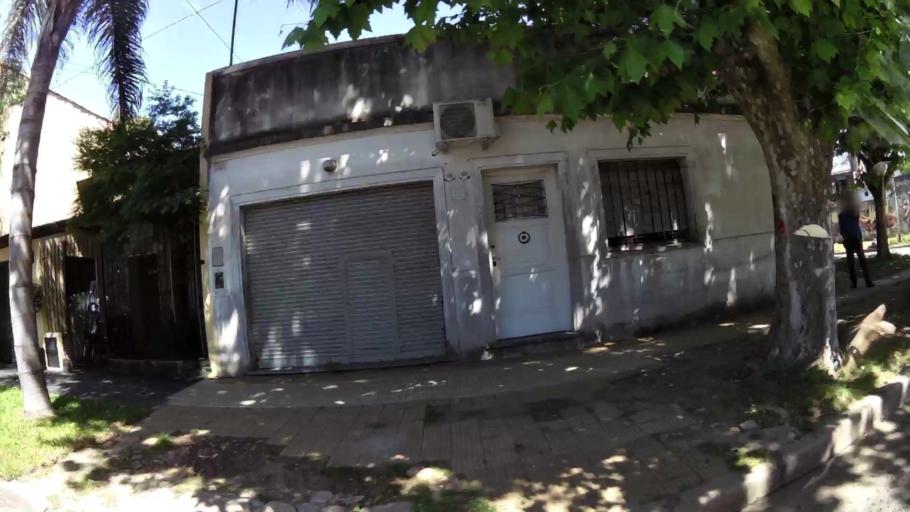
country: AR
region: Buenos Aires
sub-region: Partido de General San Martin
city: General San Martin
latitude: -34.5592
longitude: -58.5544
